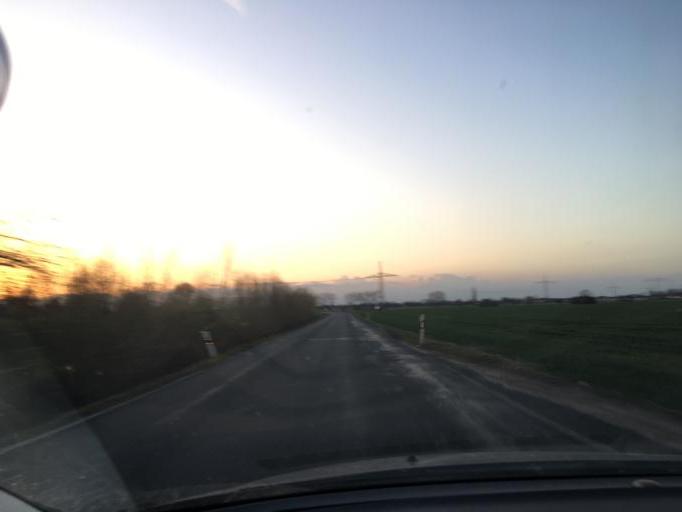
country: DE
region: Saxony
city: Borsdorf
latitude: 51.3252
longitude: 12.5337
